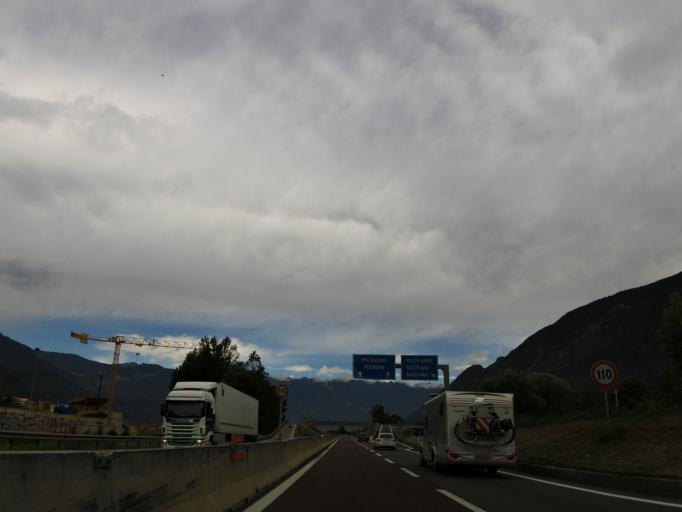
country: IT
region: Trentino-Alto Adige
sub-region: Bolzano
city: Nalles
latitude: 46.5526
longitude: 11.2188
